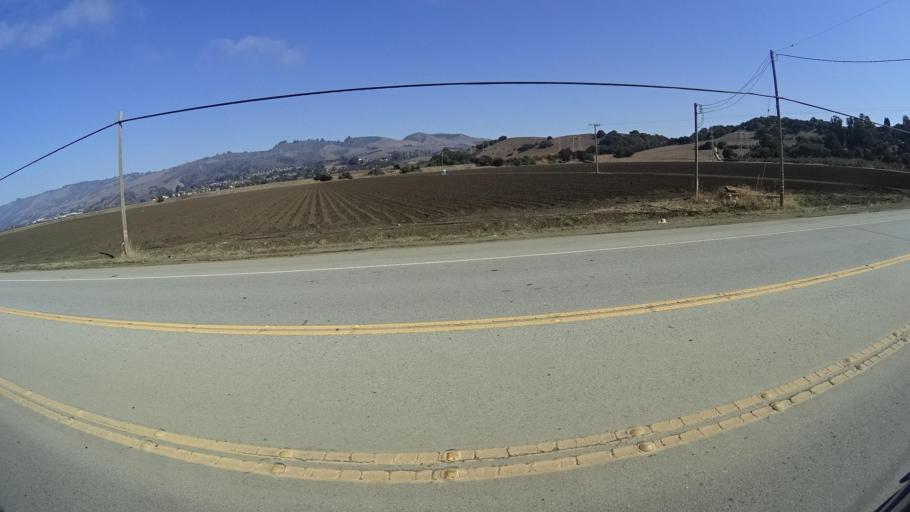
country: US
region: California
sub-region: San Benito County
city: Aromas
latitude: 36.8891
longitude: -121.6689
